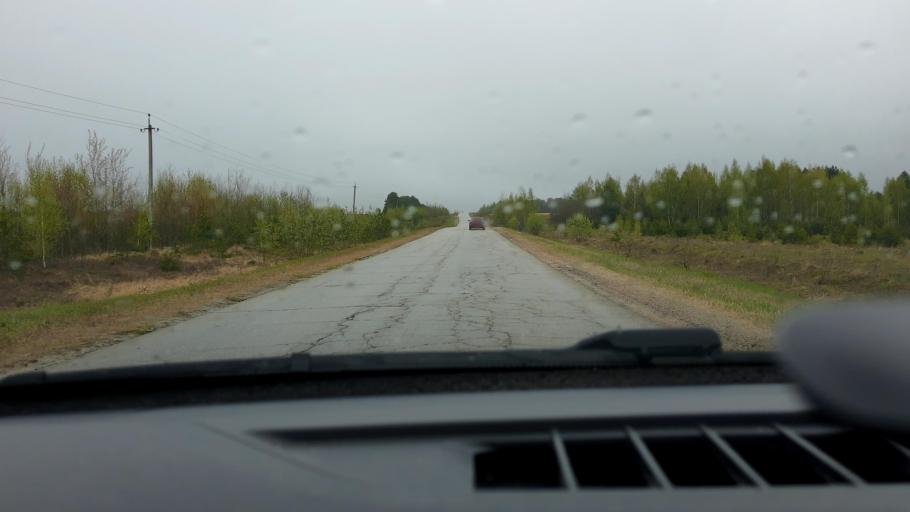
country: RU
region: Nizjnij Novgorod
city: Perevoz
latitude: 55.6796
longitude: 44.4396
